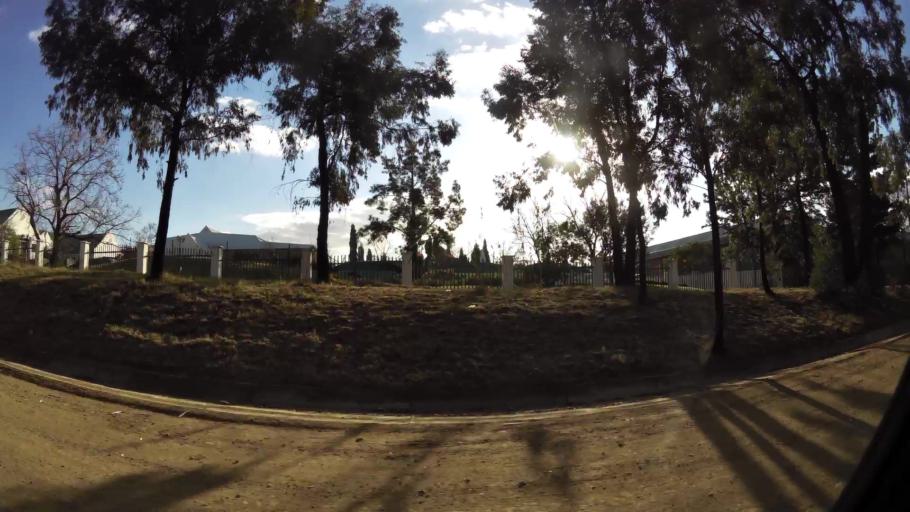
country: ZA
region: Gauteng
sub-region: City of Johannesburg Metropolitan Municipality
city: Midrand
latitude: -25.9702
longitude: 28.1365
